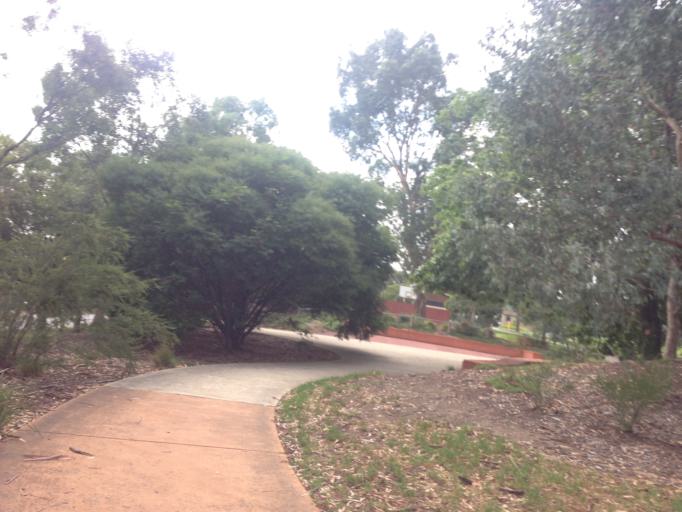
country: AU
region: Victoria
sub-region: Boroondara
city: Balwyn North
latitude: -37.7968
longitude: 145.0924
